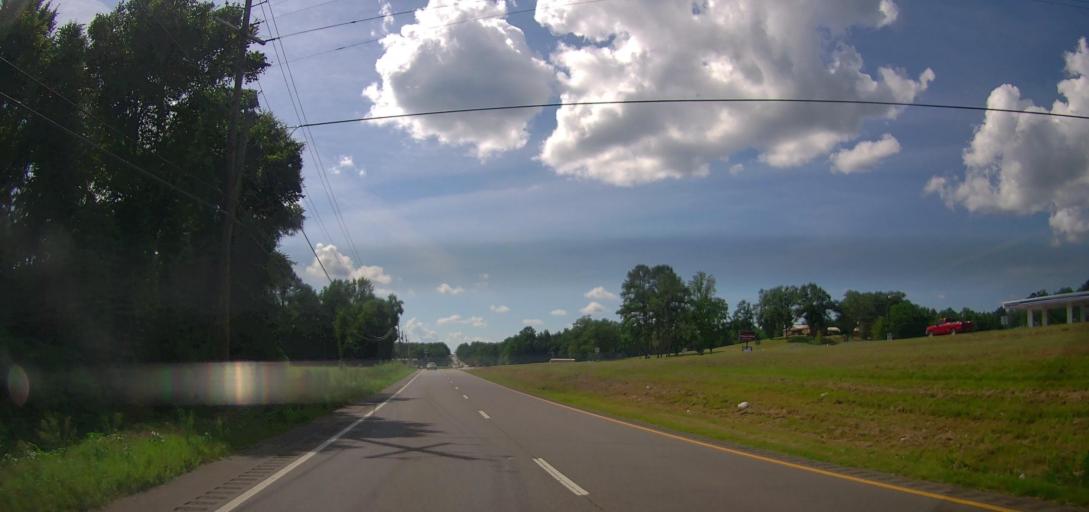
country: US
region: Alabama
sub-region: Tuscaloosa County
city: Northport
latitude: 33.2436
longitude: -87.6695
